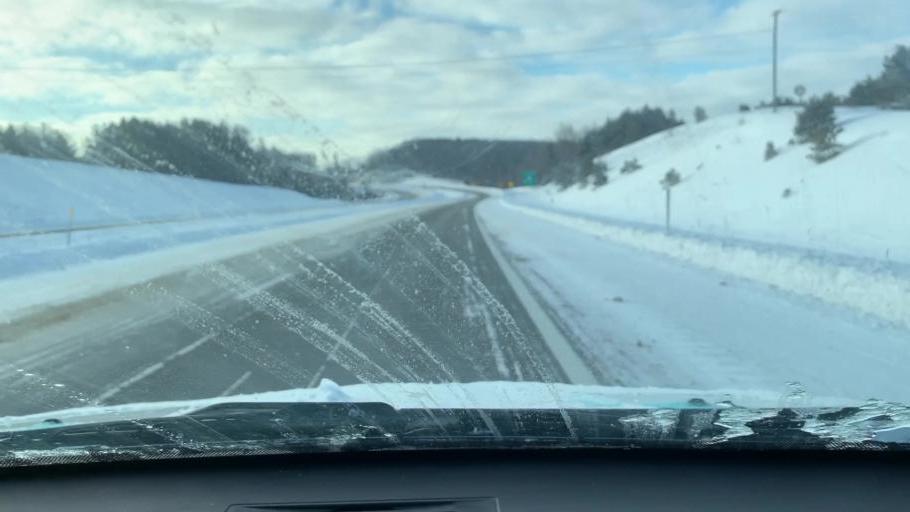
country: US
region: Michigan
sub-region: Wexford County
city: Cadillac
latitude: 44.3036
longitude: -85.3924
